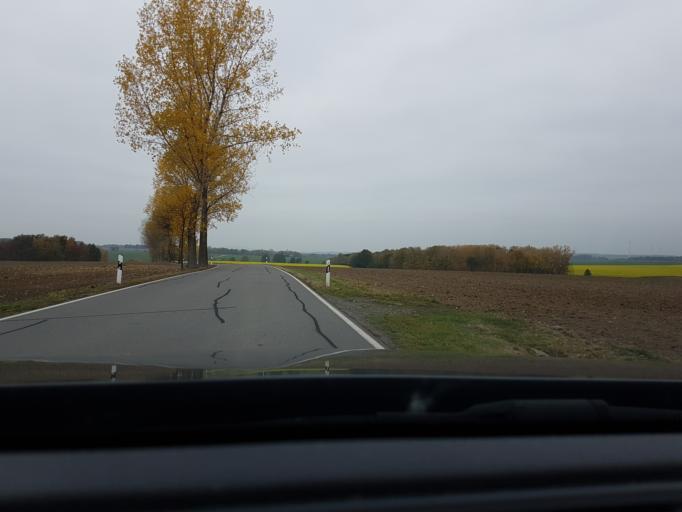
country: DE
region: Saxony
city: Altmittweida
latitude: 50.9726
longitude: 12.9486
